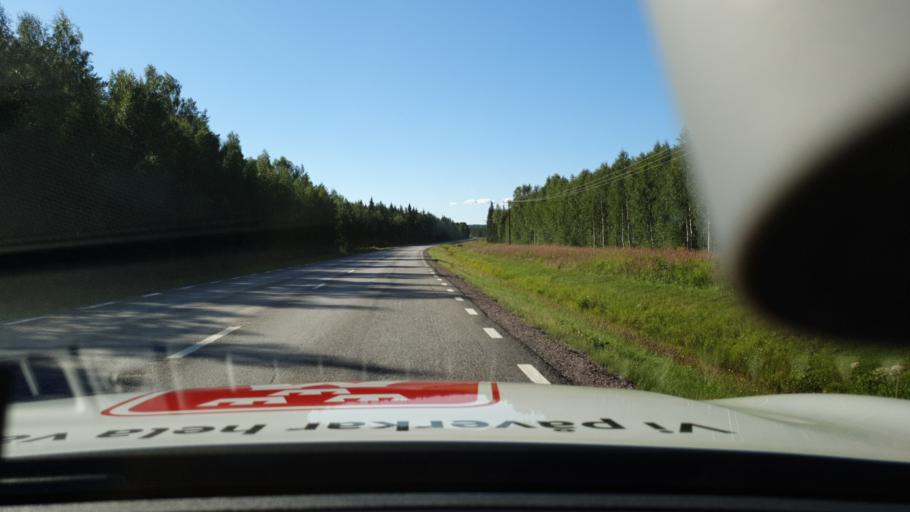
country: SE
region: Norrbotten
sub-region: Pitea Kommun
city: Rosvik
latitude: 65.5837
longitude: 21.6783
